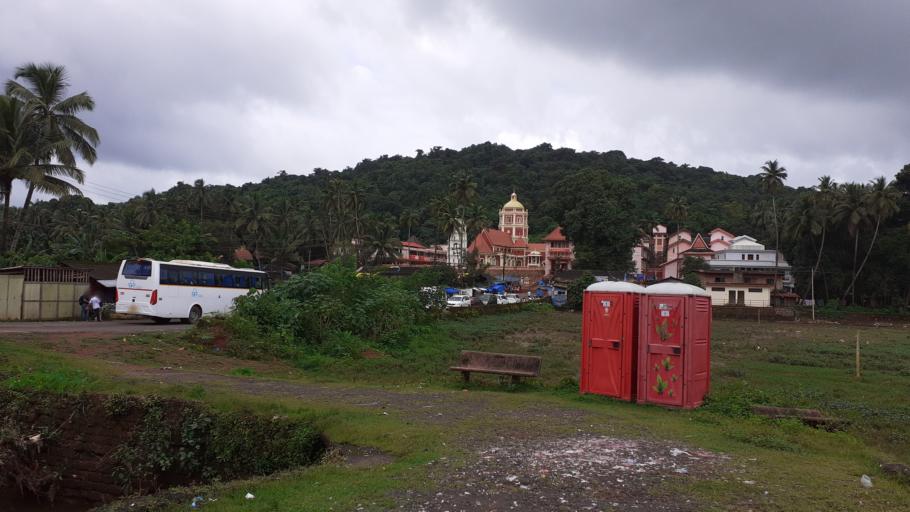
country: IN
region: Goa
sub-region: North Goa
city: Queula
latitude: 15.3971
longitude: 73.9872
